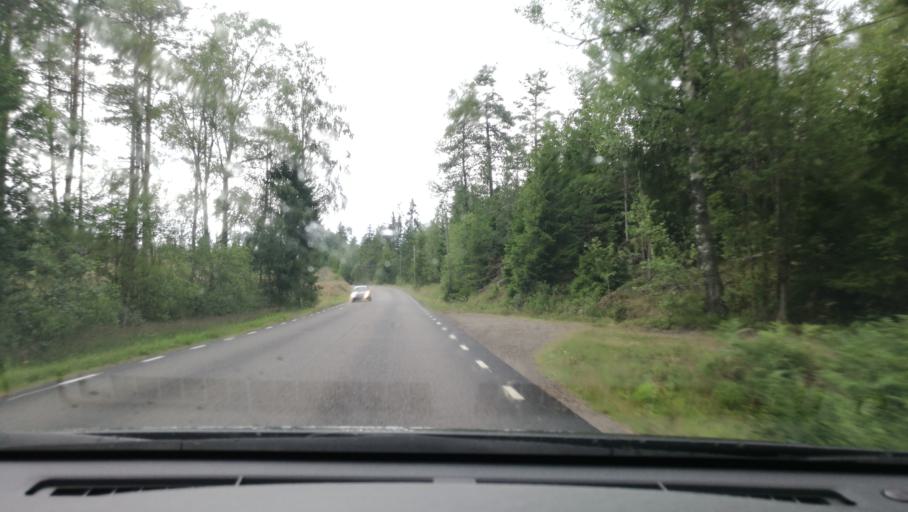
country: SE
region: OEstergoetland
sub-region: Norrkopings Kommun
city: Jursla
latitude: 58.7999
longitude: 16.1459
